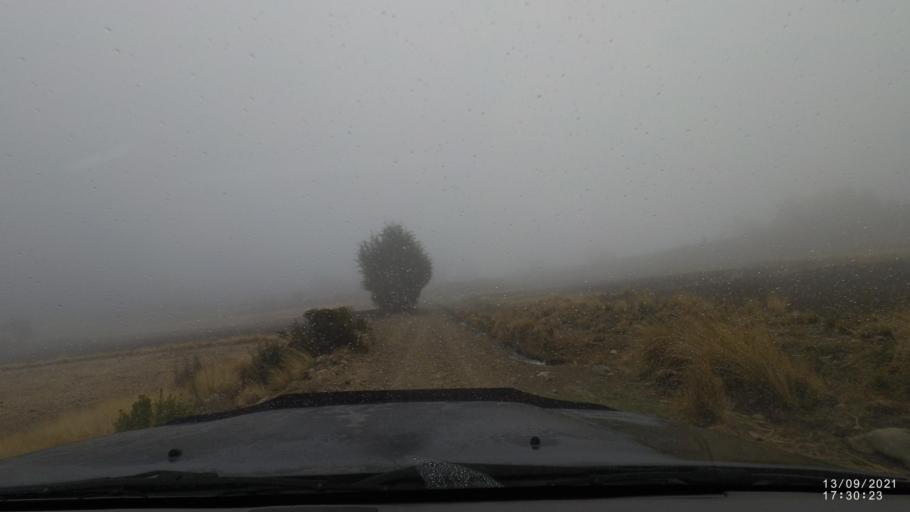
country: BO
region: Cochabamba
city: Colomi
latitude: -17.3616
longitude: -65.7863
